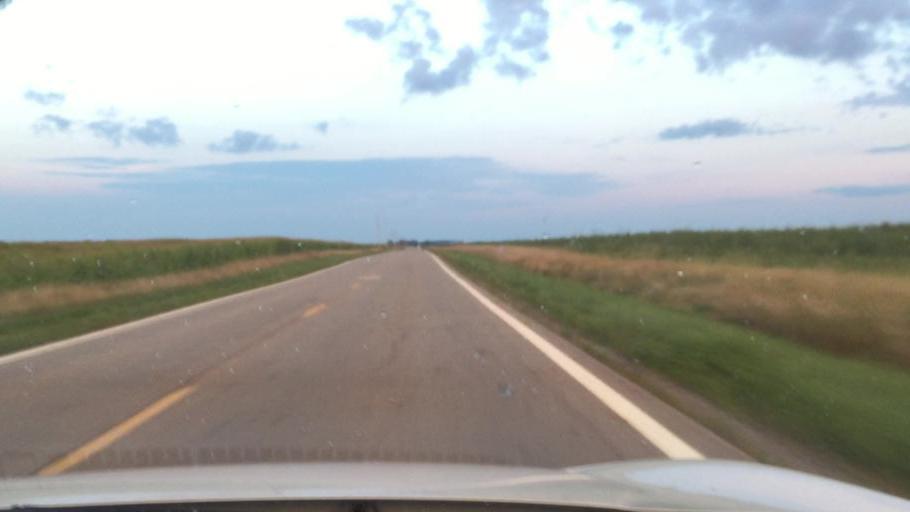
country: US
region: Ohio
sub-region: Madison County
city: Choctaw Lake
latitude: 40.0160
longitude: -83.4632
